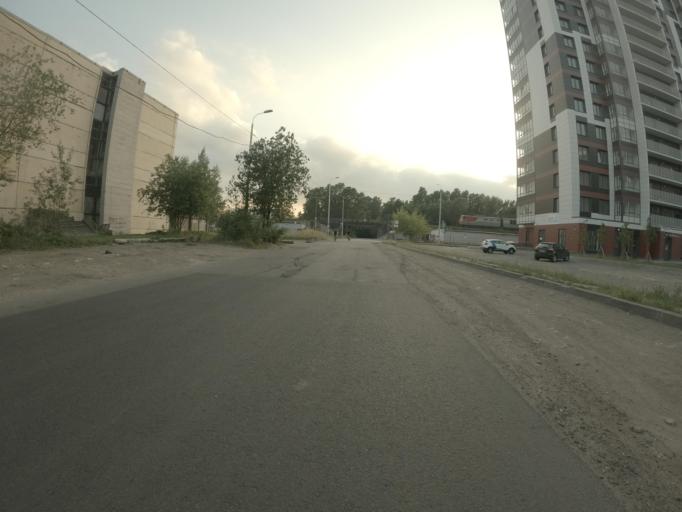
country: RU
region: St.-Petersburg
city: Krasnogvargeisky
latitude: 59.9553
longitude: 30.4485
